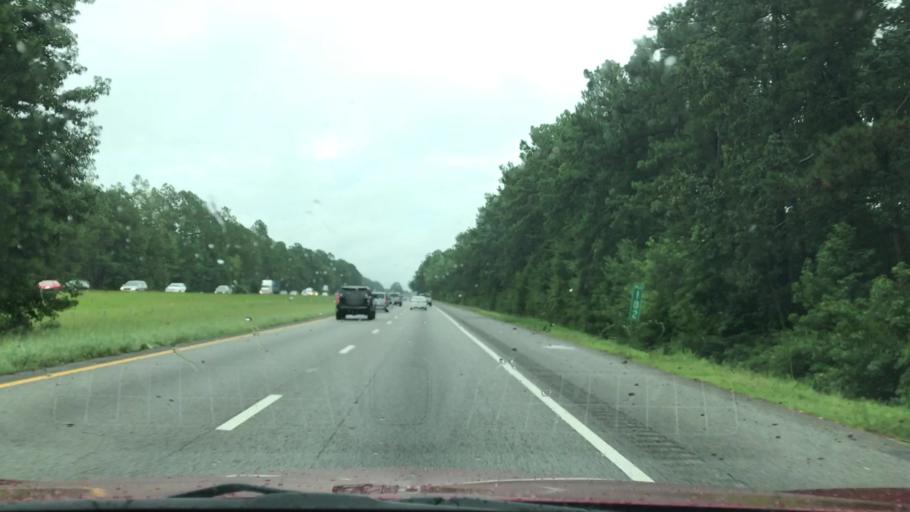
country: US
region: South Carolina
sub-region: Dorchester County
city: Ridgeville
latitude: 33.1848
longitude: -80.3832
